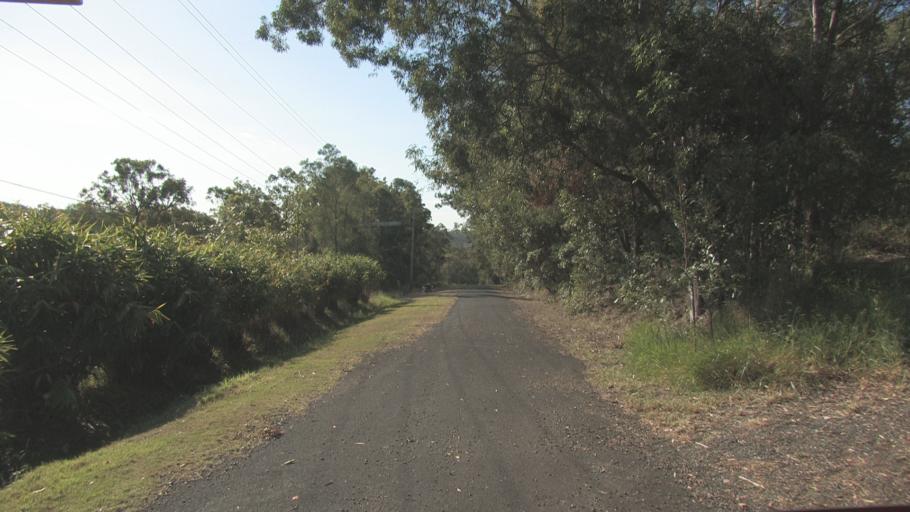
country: AU
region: Queensland
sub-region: Logan
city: Windaroo
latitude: -27.7425
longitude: 153.1648
